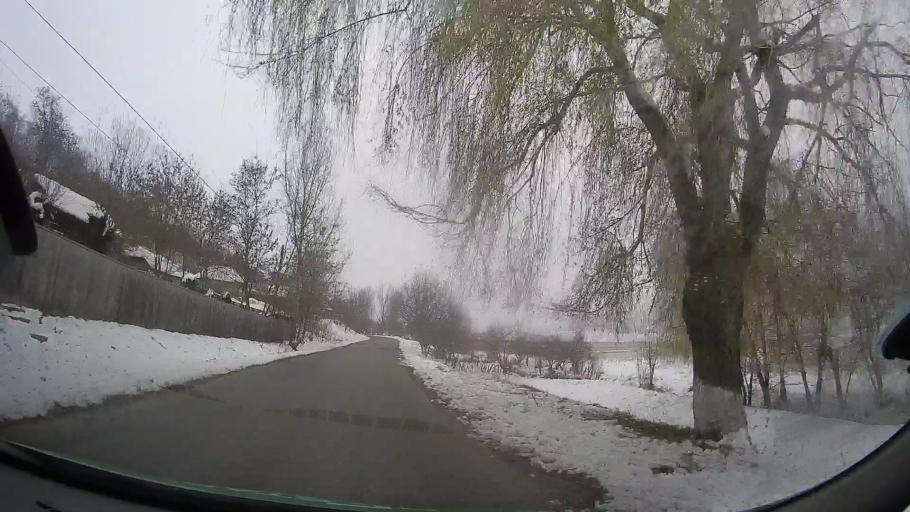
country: RO
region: Bacau
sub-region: Comuna Vultureni
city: Vultureni
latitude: 46.3580
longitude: 27.2895
